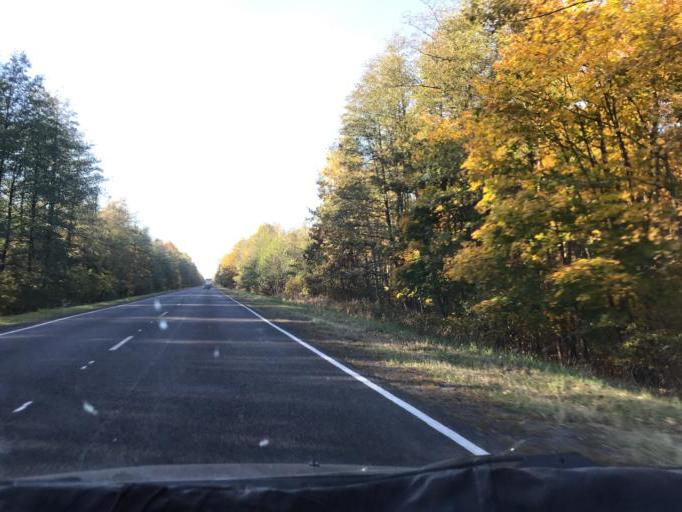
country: BY
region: Gomel
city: Mazyr
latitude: 52.1782
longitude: 29.1746
